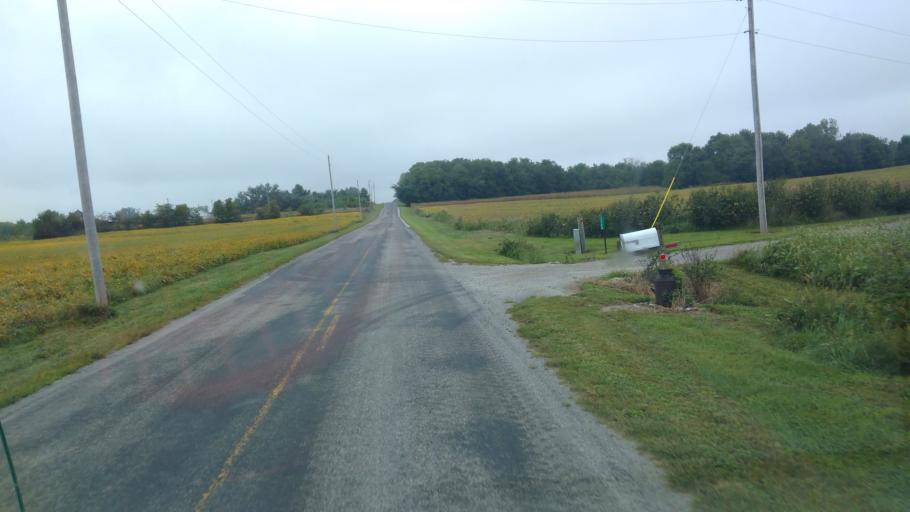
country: US
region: Ohio
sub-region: Hardin County
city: Kenton
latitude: 40.5663
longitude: -83.6363
